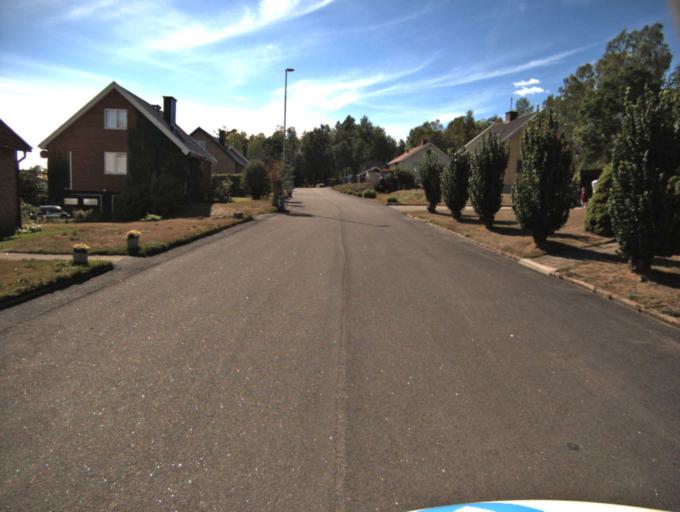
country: SE
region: Vaestra Goetaland
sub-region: Ulricehamns Kommun
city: Ulricehamn
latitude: 57.6969
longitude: 13.5711
